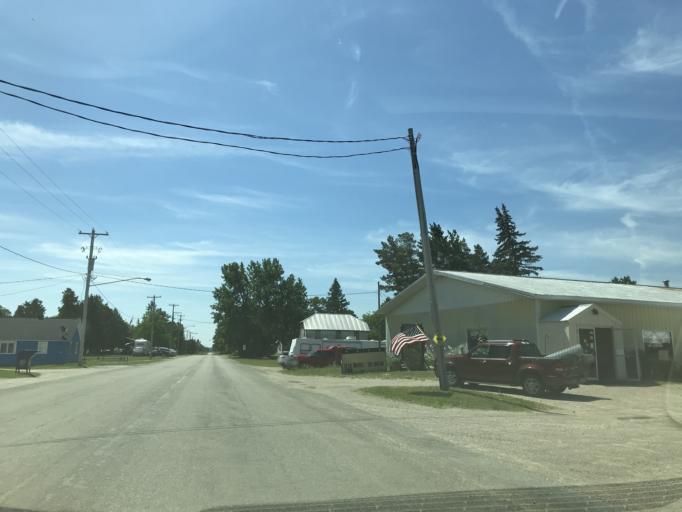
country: US
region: Michigan
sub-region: Roscommon County
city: Houghton Lake
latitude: 44.3317
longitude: -84.9446
